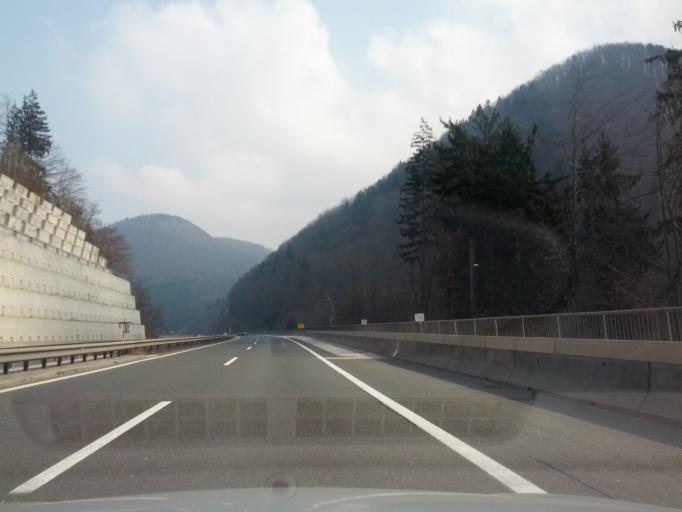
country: SI
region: Vransko
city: Vransko
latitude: 46.2177
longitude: 14.9267
